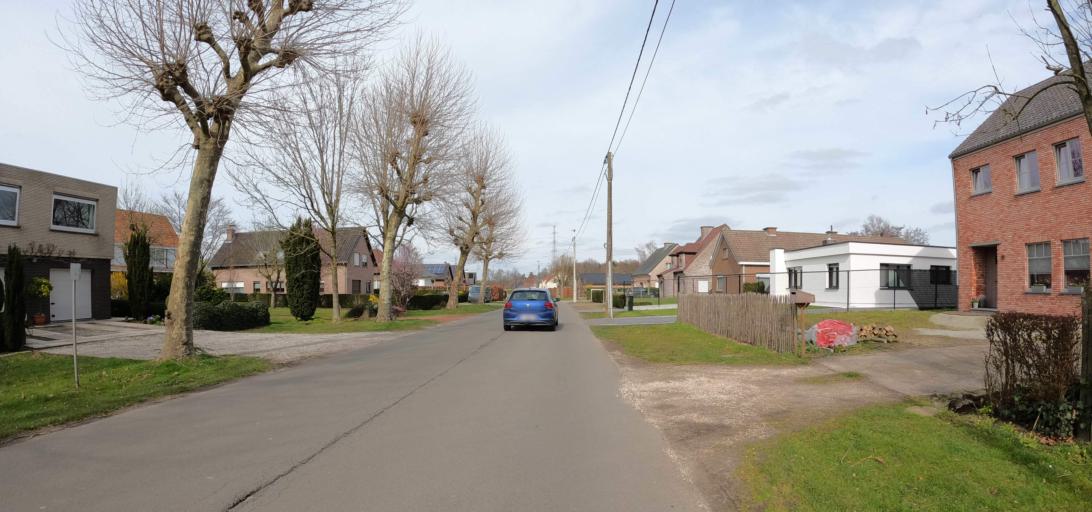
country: BE
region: Flanders
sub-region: Provincie Oost-Vlaanderen
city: Waasmunster
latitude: 51.1348
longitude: 4.0798
